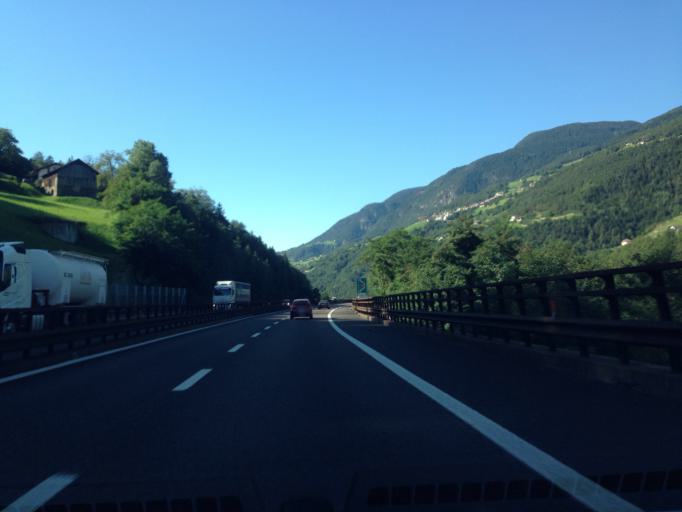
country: IT
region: Trentino-Alto Adige
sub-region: Bolzano
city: Villandro
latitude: 46.6221
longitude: 11.5455
